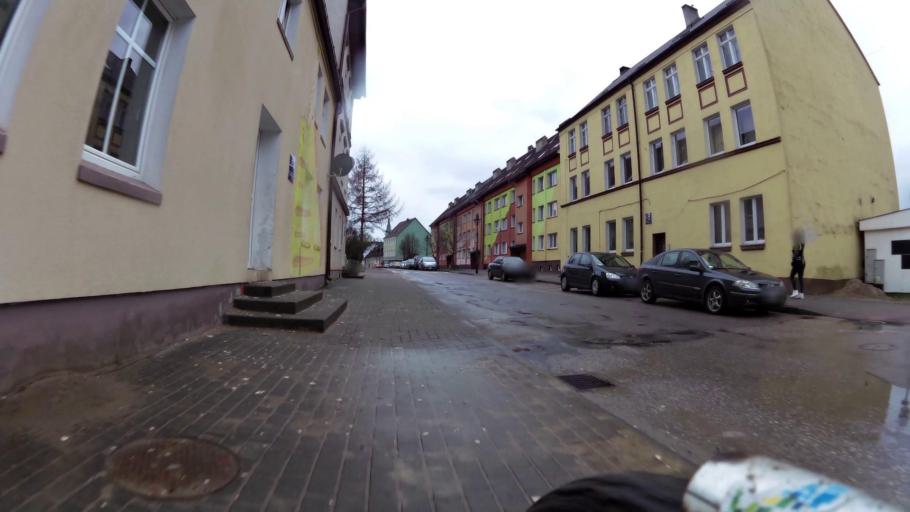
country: PL
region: Pomeranian Voivodeship
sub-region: Powiat bytowski
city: Miastko
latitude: 54.0057
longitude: 16.9814
